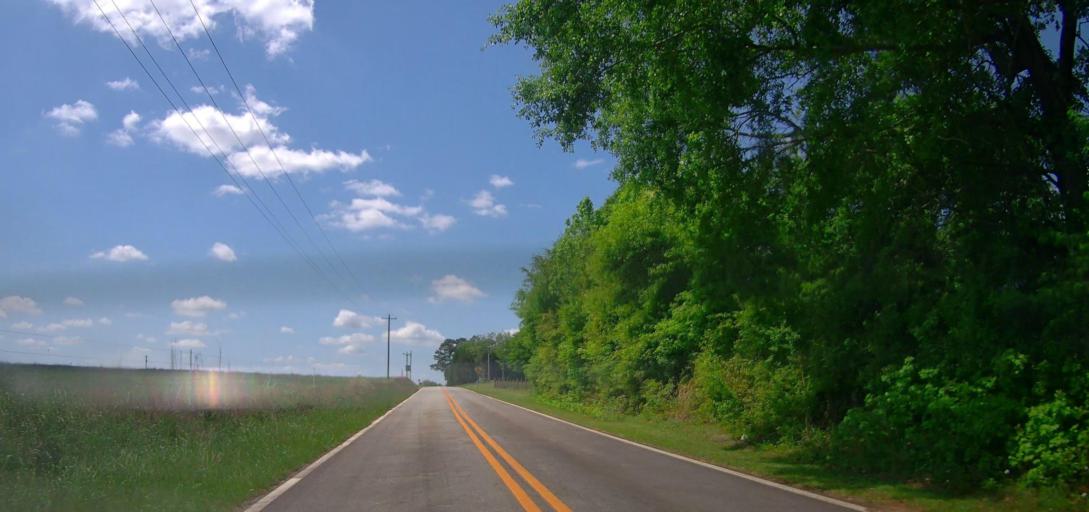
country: US
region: Georgia
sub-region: Putnam County
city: Eatonton
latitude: 33.3337
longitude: -83.3219
